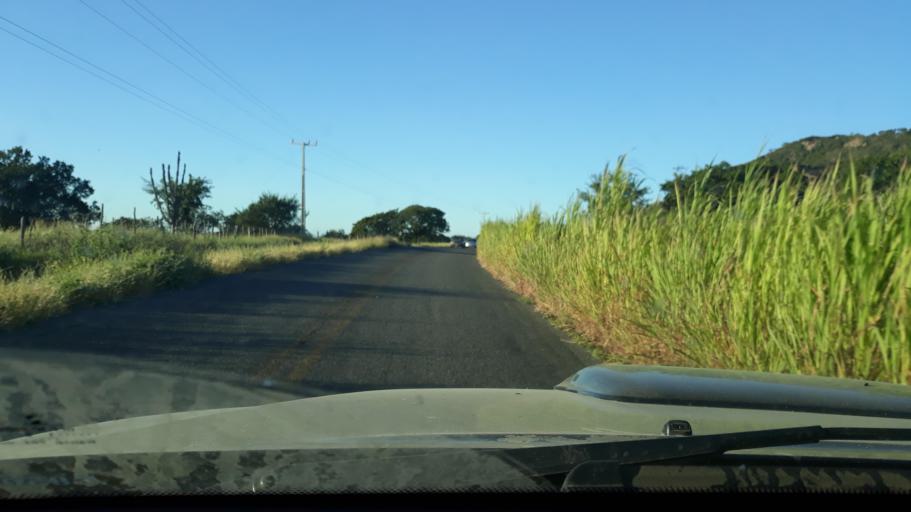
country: BR
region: Bahia
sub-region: Guanambi
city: Guanambi
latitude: -14.0481
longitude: -42.8734
